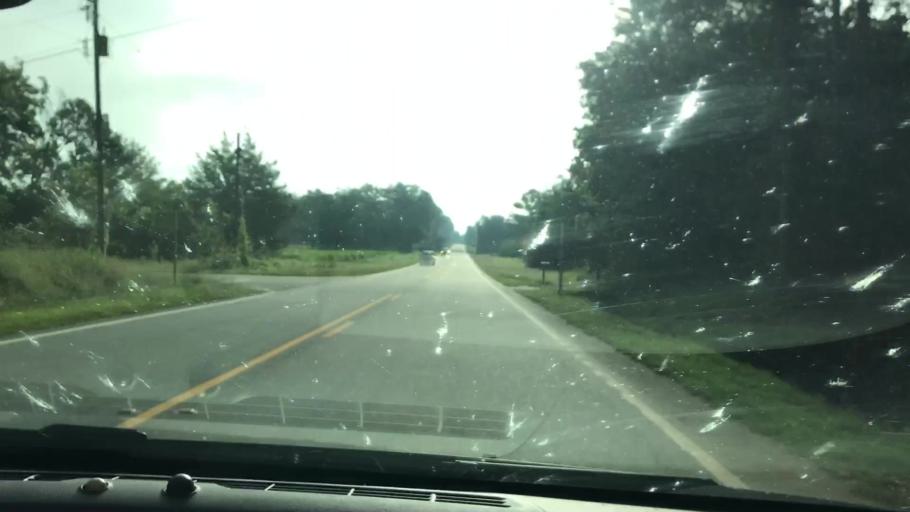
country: US
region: Georgia
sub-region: Terrell County
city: Dawson
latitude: 31.7704
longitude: -84.5312
